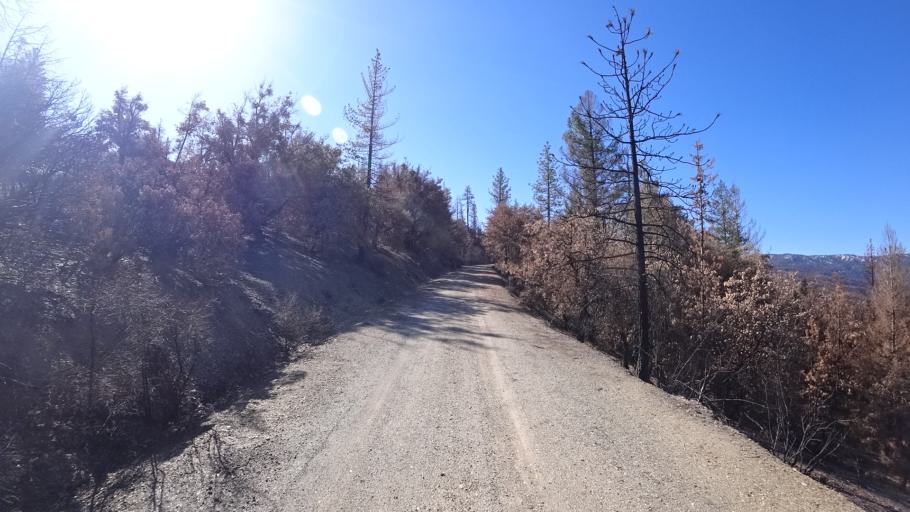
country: US
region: California
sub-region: Tehama County
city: Rancho Tehama Reserve
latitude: 39.6776
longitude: -122.7089
